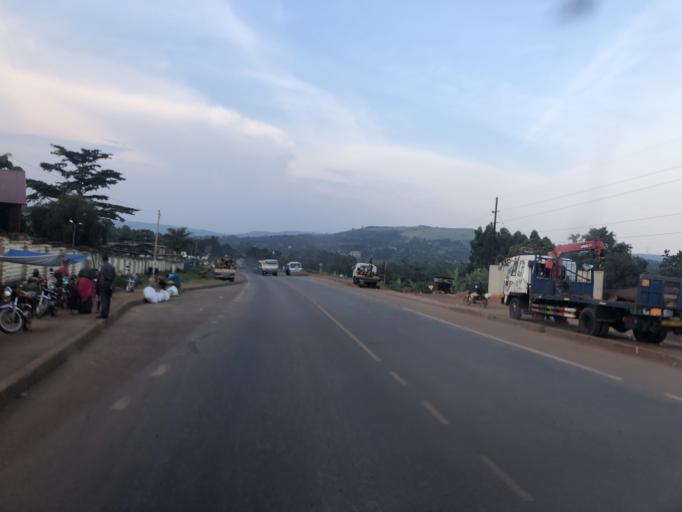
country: UG
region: Central Region
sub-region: Mpigi District
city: Mpigi
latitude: 0.2193
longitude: 32.3335
